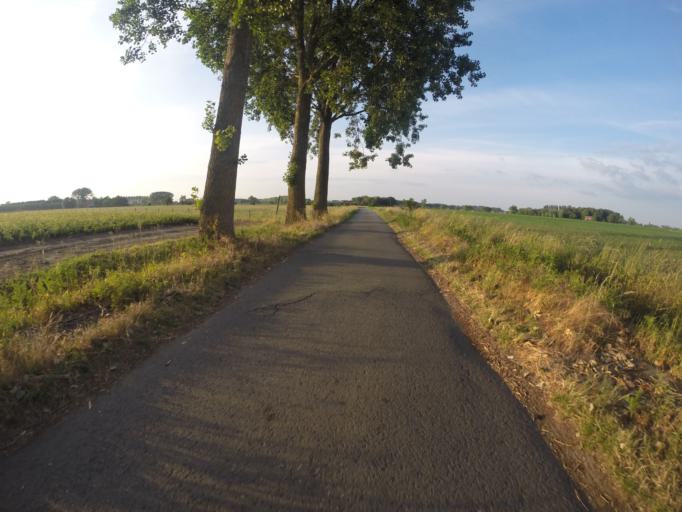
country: BE
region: Flanders
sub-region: Provincie West-Vlaanderen
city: Beernem
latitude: 51.1446
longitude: 3.2957
